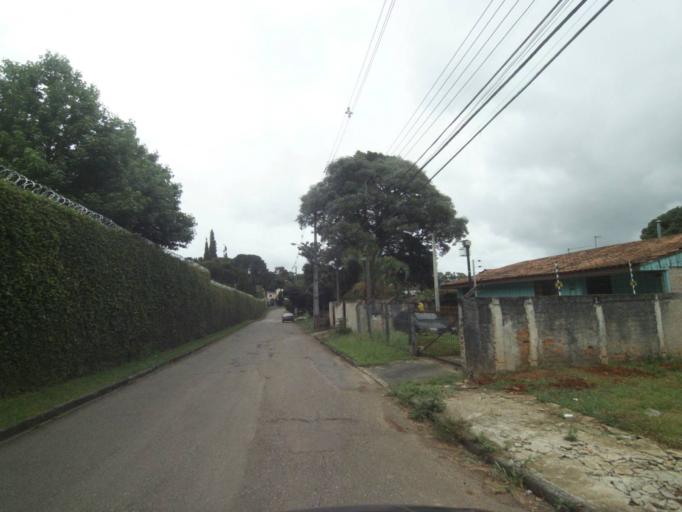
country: BR
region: Parana
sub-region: Curitiba
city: Curitiba
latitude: -25.4525
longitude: -49.3334
